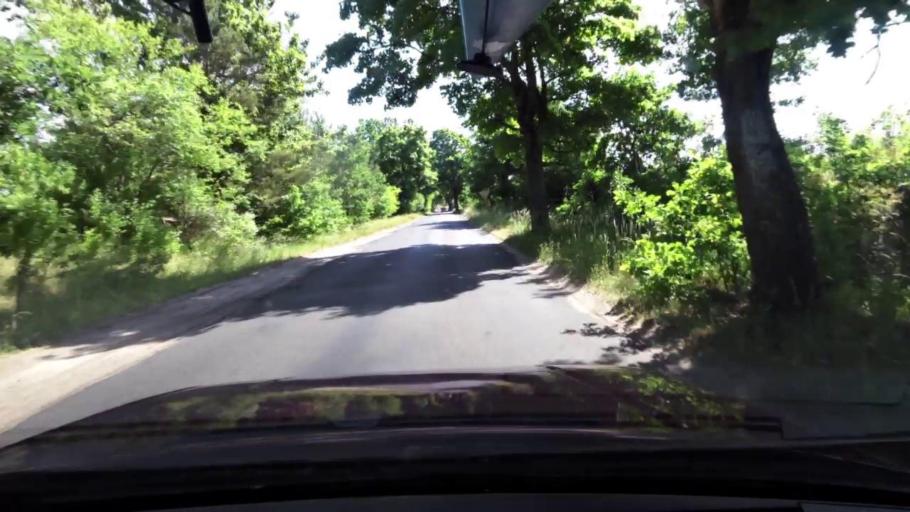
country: PL
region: Pomeranian Voivodeship
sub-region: Powiat slupski
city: Kepice
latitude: 54.2841
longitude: 16.9582
